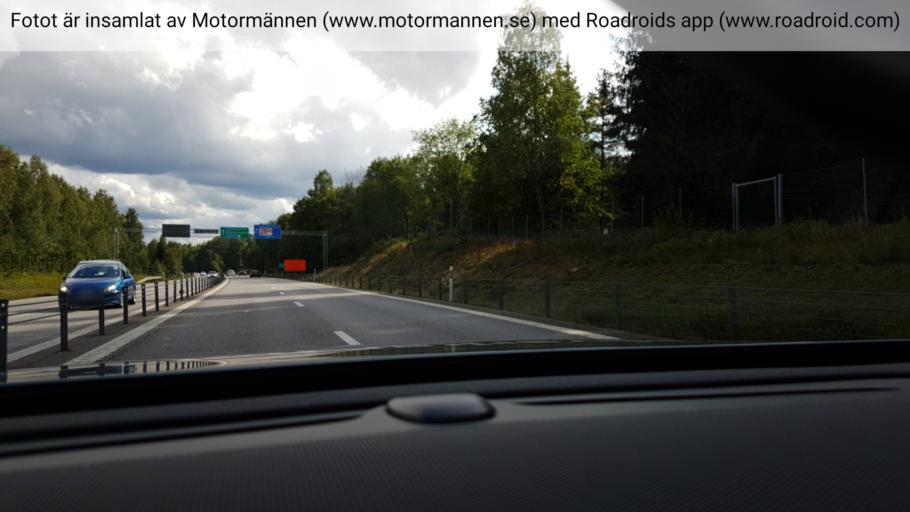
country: SE
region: Vaestra Goetaland
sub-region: Trollhattan
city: Trollhattan
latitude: 58.3265
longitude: 12.2986
